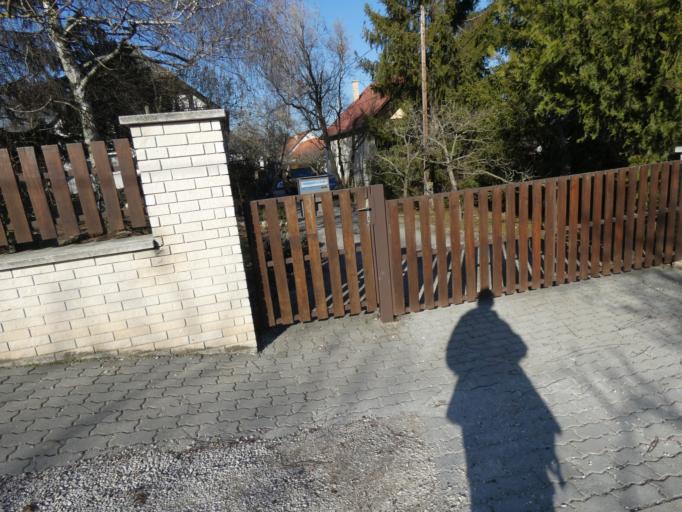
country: HU
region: Pest
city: Solymar
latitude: 47.5893
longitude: 18.9239
